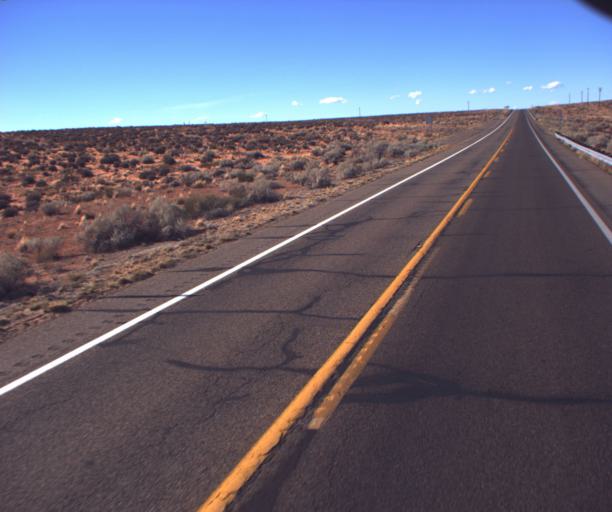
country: US
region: Arizona
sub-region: Coconino County
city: Page
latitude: 36.9541
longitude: -111.5006
